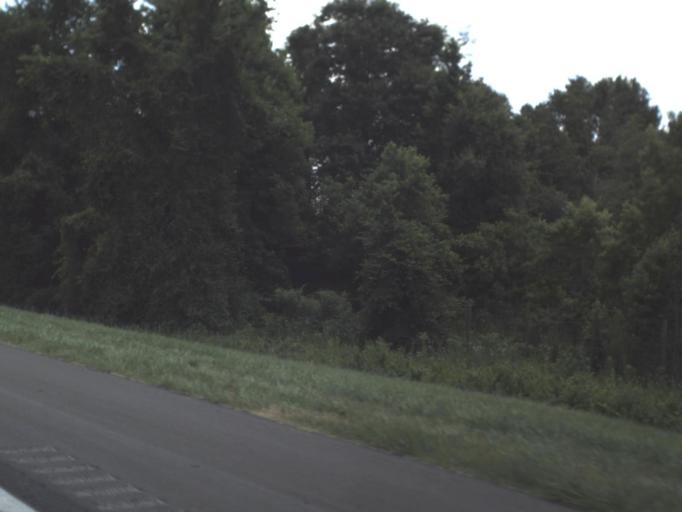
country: US
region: Florida
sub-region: Madison County
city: Madison
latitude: 30.4142
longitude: -83.4330
